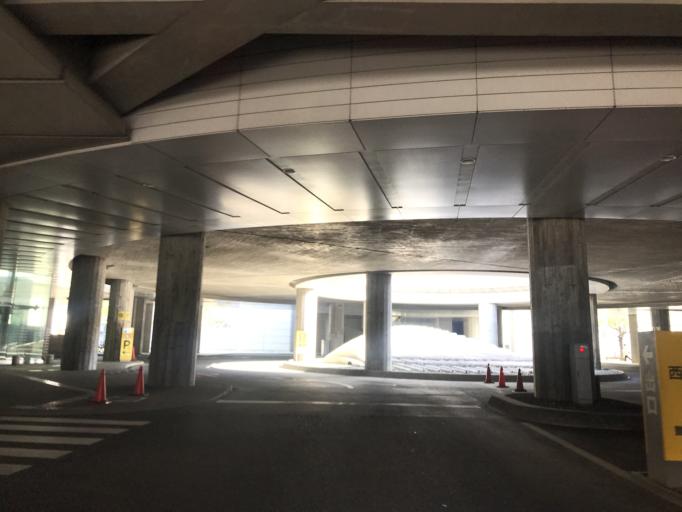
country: JP
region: Ibaraki
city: Mito-shi
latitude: 36.3409
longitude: 140.4465
